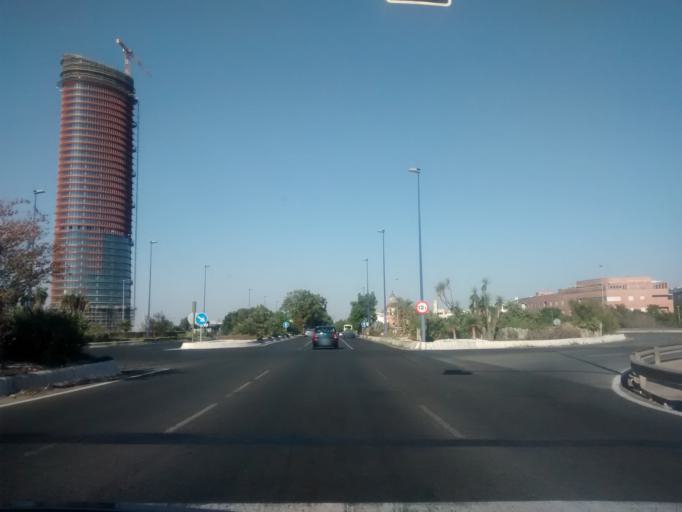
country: ES
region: Andalusia
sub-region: Provincia de Sevilla
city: Camas
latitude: 37.3893
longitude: -6.0145
